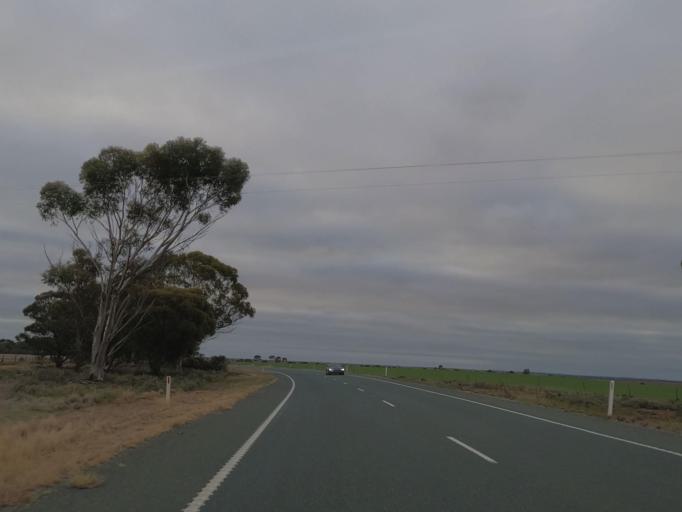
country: AU
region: Victoria
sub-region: Swan Hill
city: Swan Hill
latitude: -35.5633
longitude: 143.7828
